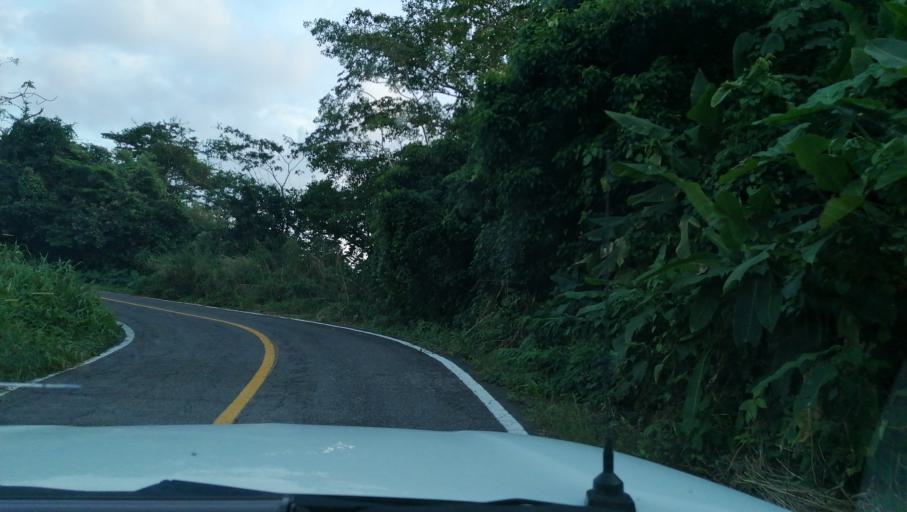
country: MX
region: Chiapas
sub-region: Juarez
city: El Triunfo 1ra. Seccion (Cardona)
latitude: 17.5062
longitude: -93.2273
